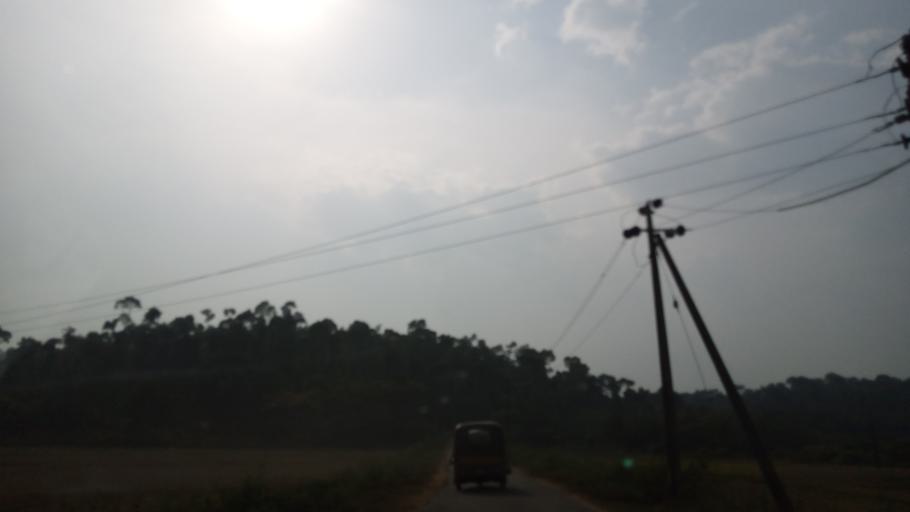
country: IN
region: Karnataka
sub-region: Chikmagalur
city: Mudigere
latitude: 13.0561
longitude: 75.6568
